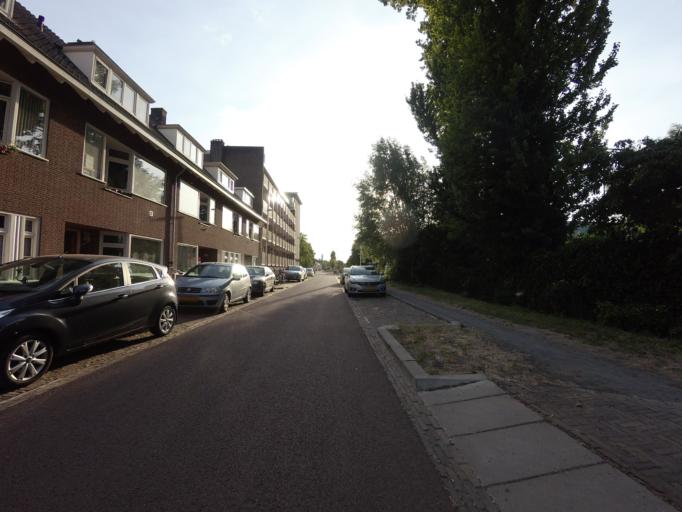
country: NL
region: Utrecht
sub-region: Gemeente Utrecht
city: Utrecht
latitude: 52.0961
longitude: 5.0971
